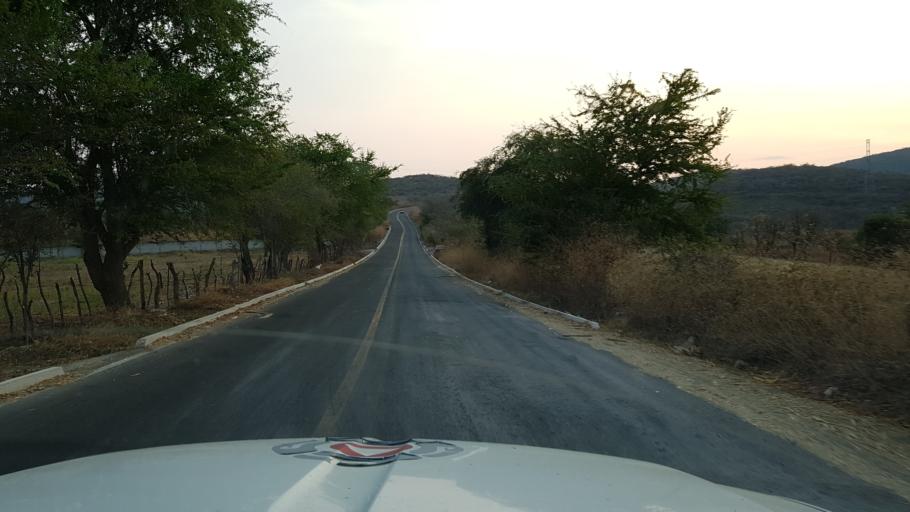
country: MX
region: Morelos
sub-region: Ayala
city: Olintepec
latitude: 18.7358
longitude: -99.0096
